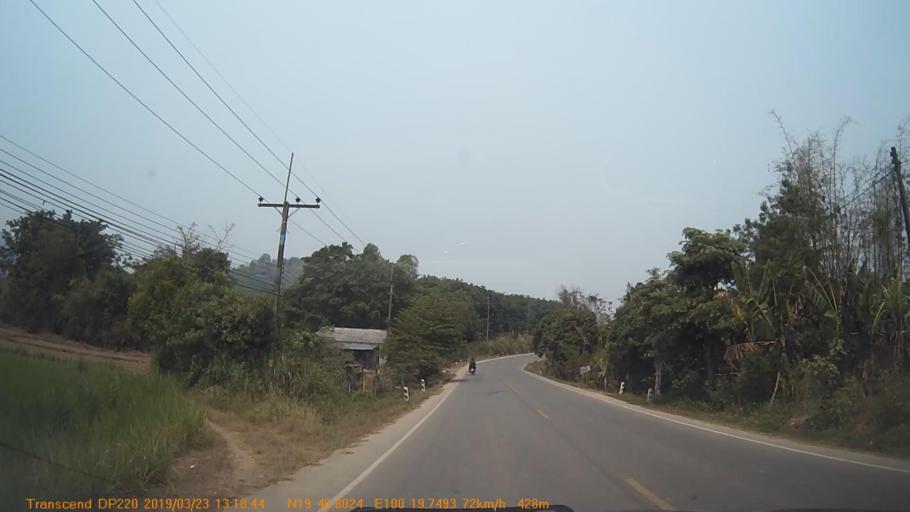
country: TH
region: Chiang Rai
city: Khun Tan
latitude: 19.7804
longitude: 100.3293
